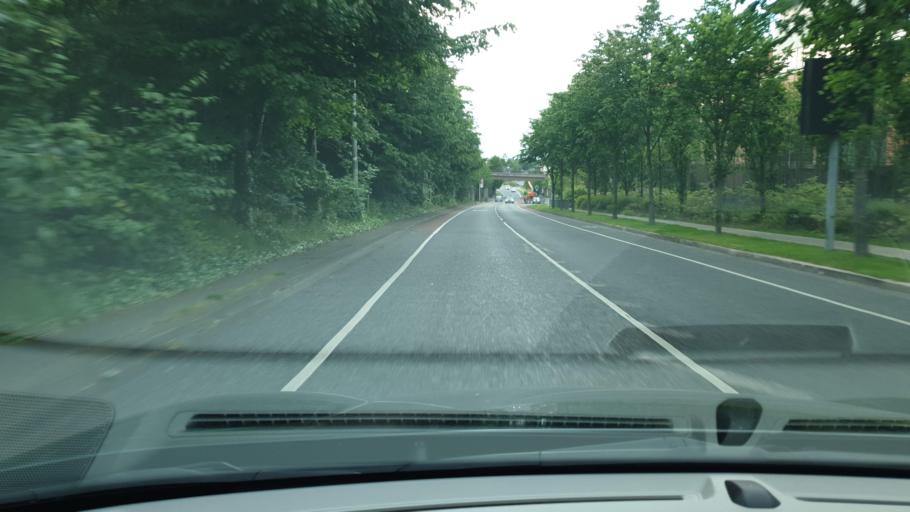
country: IE
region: Leinster
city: Balally
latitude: 53.2870
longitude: -6.2433
